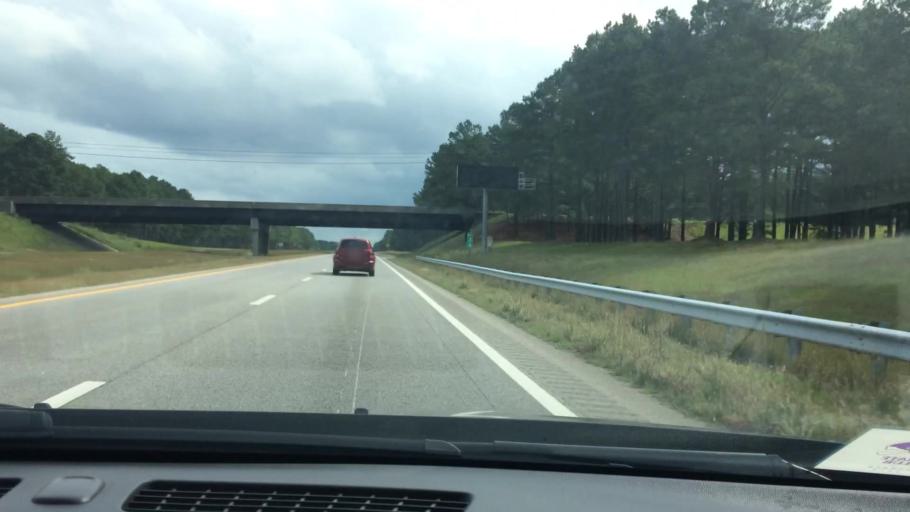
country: US
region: North Carolina
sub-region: Wilson County
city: Lucama
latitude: 35.7743
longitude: -78.0593
